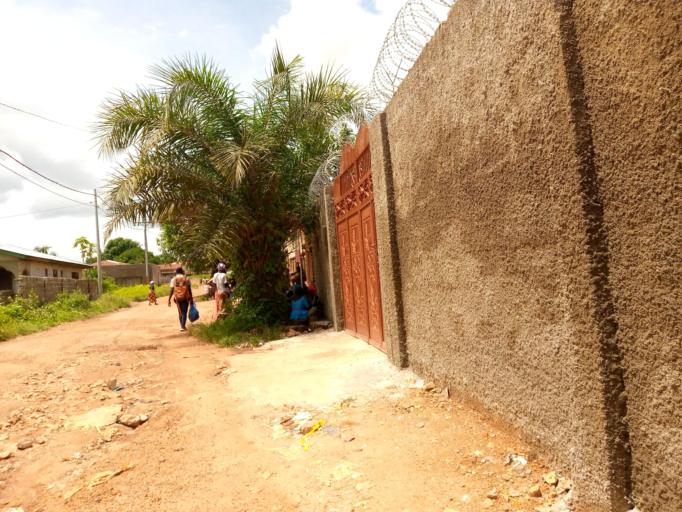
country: SL
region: Northern Province
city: Magburaka
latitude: 8.7247
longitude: -11.9378
